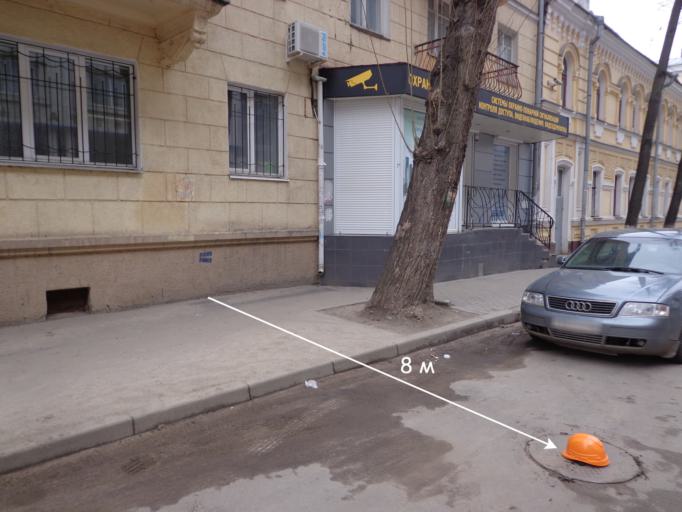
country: RU
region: Voronezj
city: Voronezh
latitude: 51.6730
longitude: 39.2026
